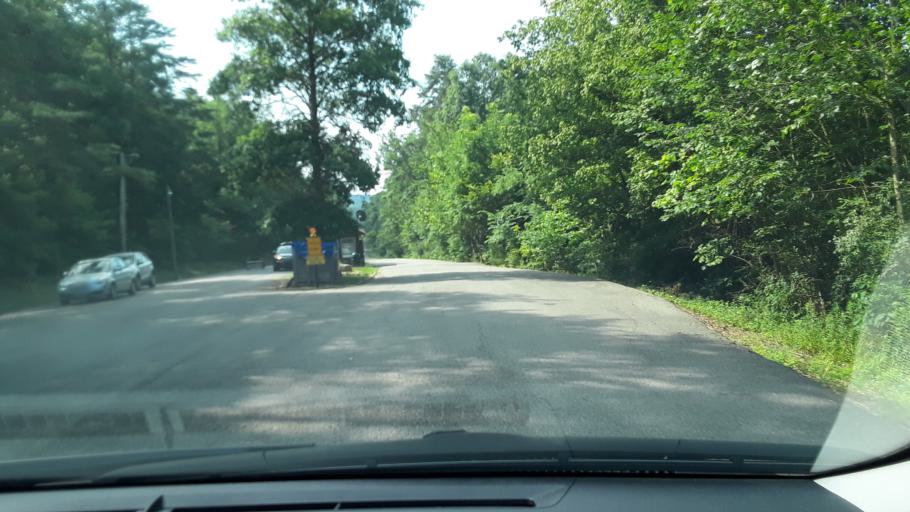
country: US
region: Indiana
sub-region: Clark County
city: Henryville
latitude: 38.4623
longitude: -85.8655
